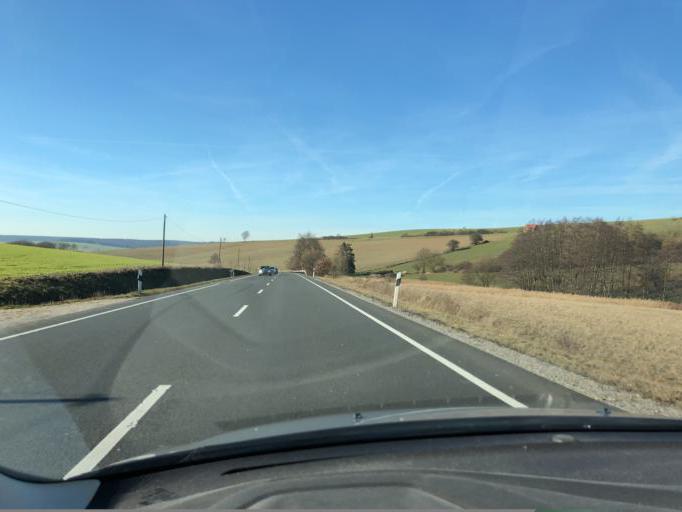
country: DE
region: Lower Saxony
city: Hahausen
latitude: 51.9489
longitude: 10.1625
